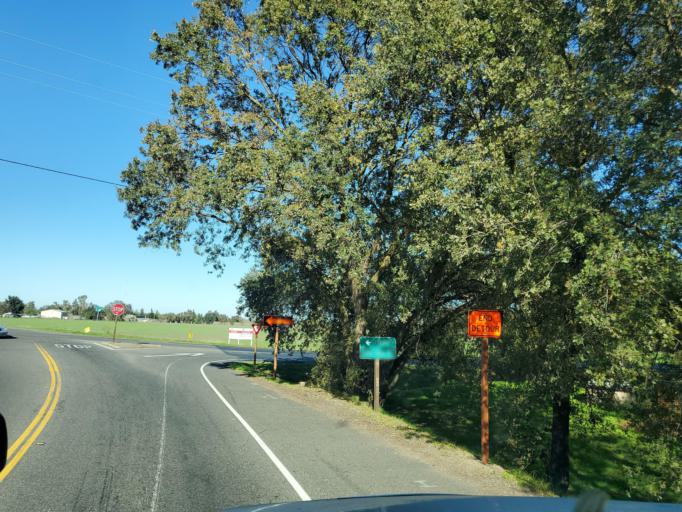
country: US
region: California
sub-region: San Joaquin County
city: Morada
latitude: 38.0570
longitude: -121.2574
